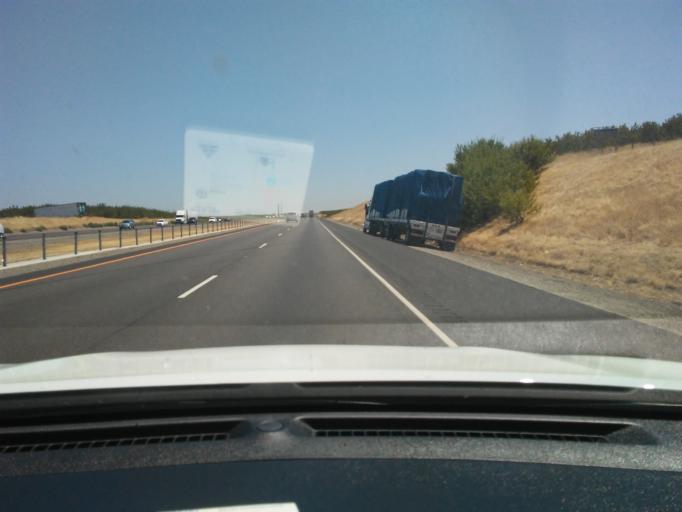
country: US
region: California
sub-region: Stanislaus County
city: Patterson
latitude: 37.5227
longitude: -121.2467
